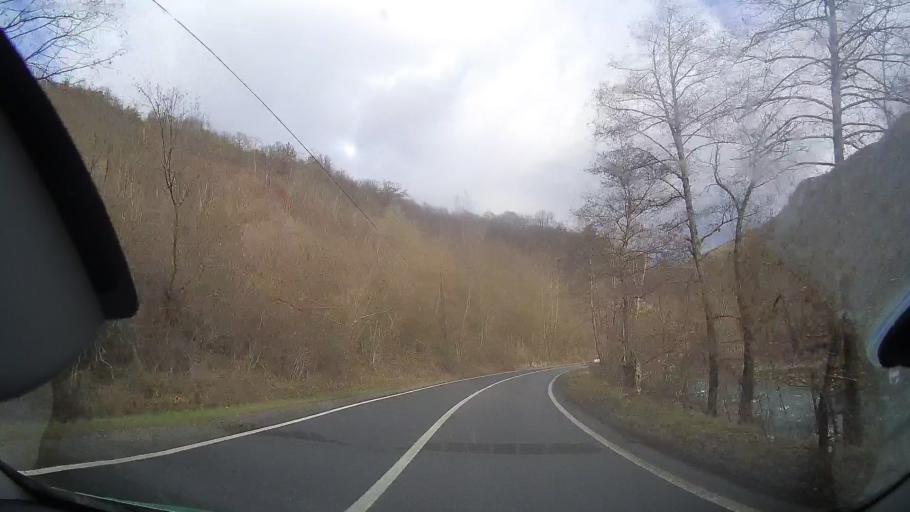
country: RO
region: Alba
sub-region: Comuna Rimetea
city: Rimetea
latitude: 46.4877
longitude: 23.5255
